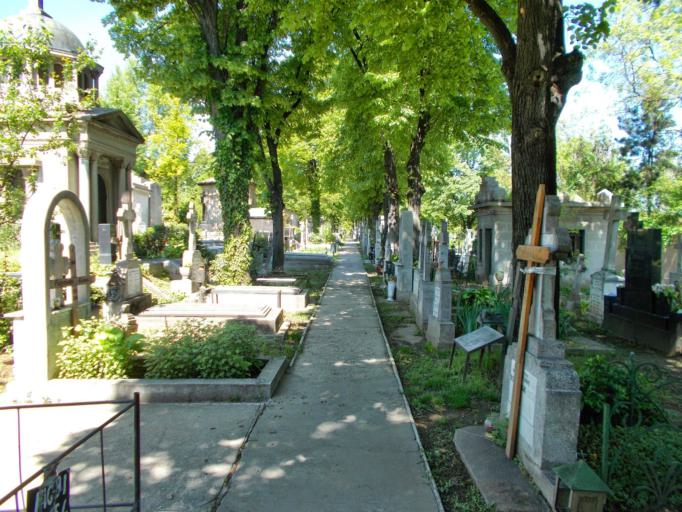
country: RO
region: Bucuresti
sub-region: Municipiul Bucuresti
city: Bucuresti
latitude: 44.4043
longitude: 26.1013
